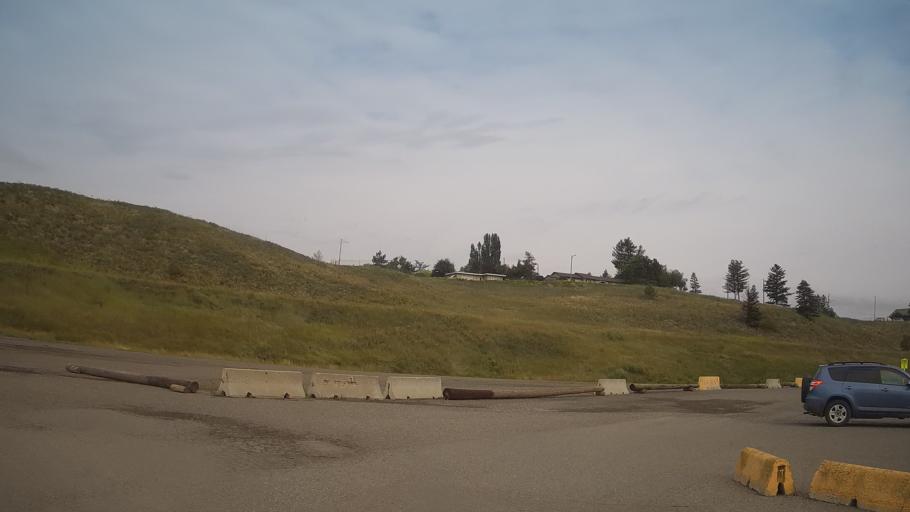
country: CA
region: British Columbia
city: Williams Lake
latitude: 52.1248
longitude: -122.1329
